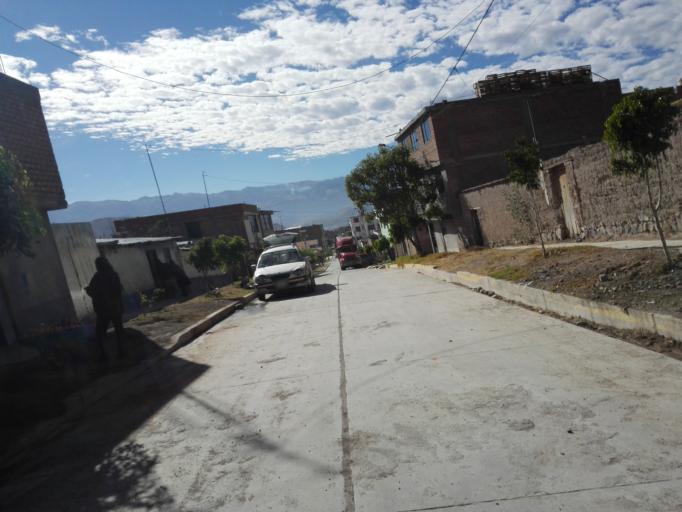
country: PE
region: Ayacucho
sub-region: Provincia de Huamanga
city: Ayacucho
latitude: -13.1363
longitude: -74.2338
